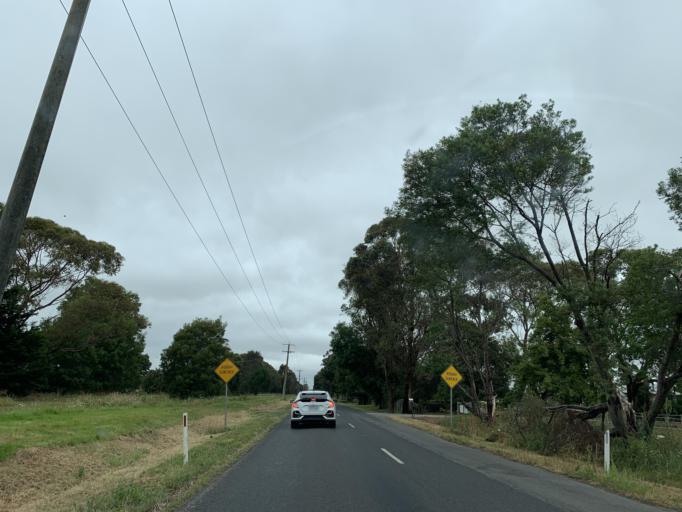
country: AU
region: Victoria
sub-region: Cardinia
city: Pakenham South
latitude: -38.1662
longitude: 145.5443
